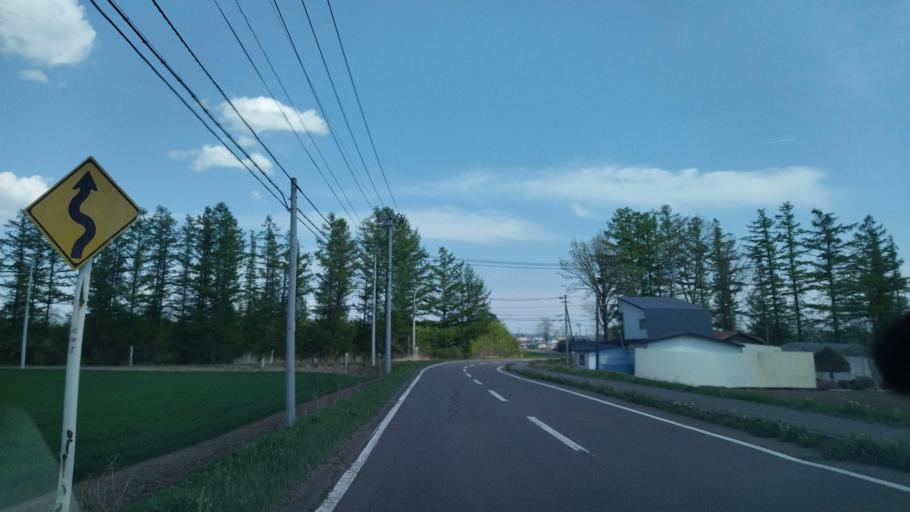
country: JP
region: Hokkaido
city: Otofuke
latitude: 43.1003
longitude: 143.2235
